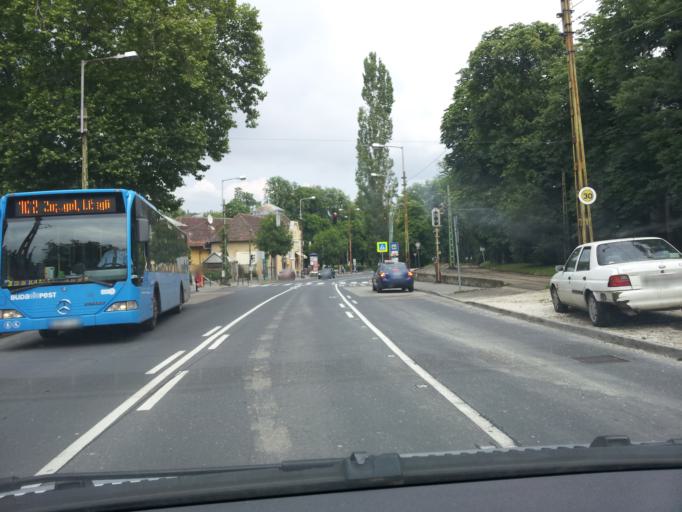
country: HU
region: Budapest
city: Budapest XII. keruelet
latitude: 47.5176
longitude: 18.9946
